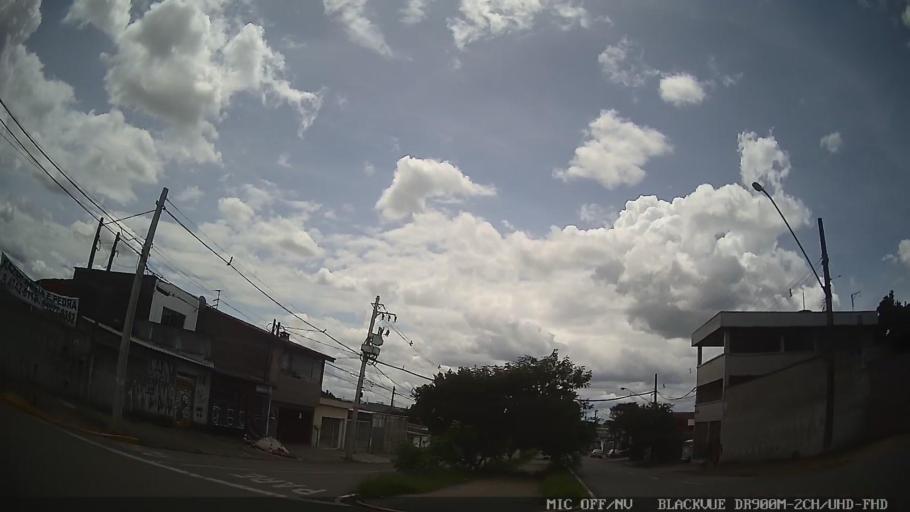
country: BR
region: Sao Paulo
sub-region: Mogi das Cruzes
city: Mogi das Cruzes
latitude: -23.5774
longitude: -46.2223
